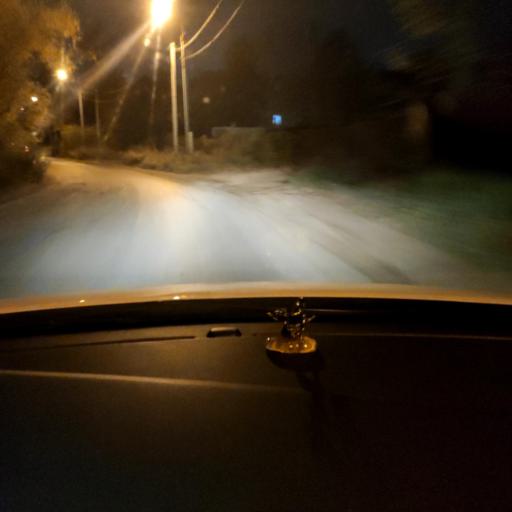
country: RU
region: Tatarstan
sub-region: Gorod Kazan'
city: Kazan
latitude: 55.7263
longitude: 49.1580
